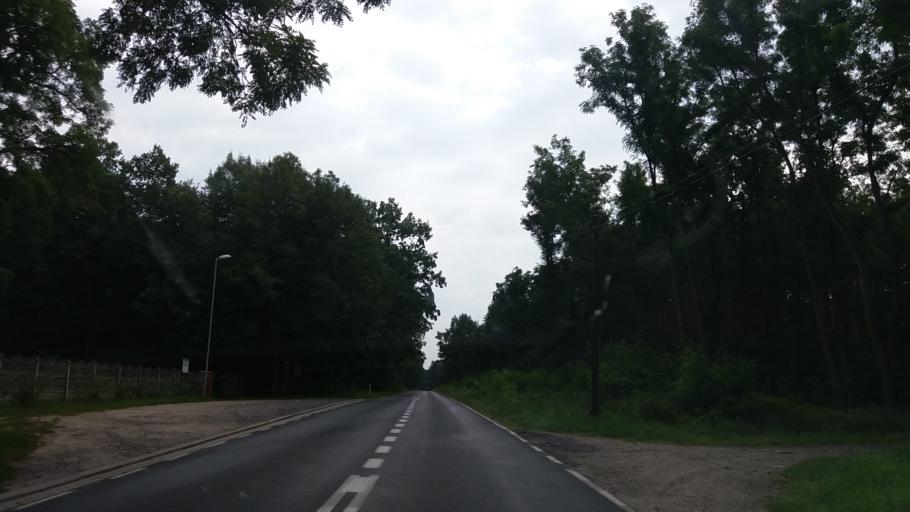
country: PL
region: Lubusz
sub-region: Powiat miedzyrzecki
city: Skwierzyna
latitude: 52.6391
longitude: 15.4533
